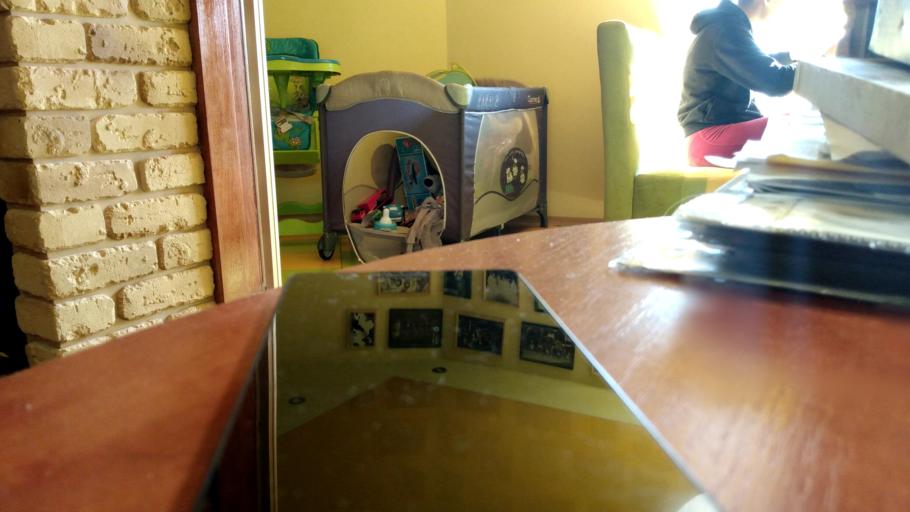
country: RU
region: Penza
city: Serdobsk
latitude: 52.3609
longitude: 44.3552
